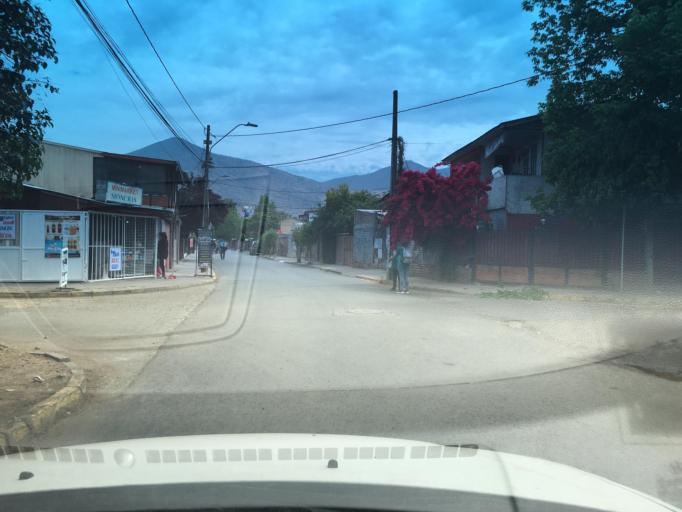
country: CL
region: Santiago Metropolitan
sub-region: Provincia de Santiago
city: Santiago
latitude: -33.3838
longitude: -70.6450
